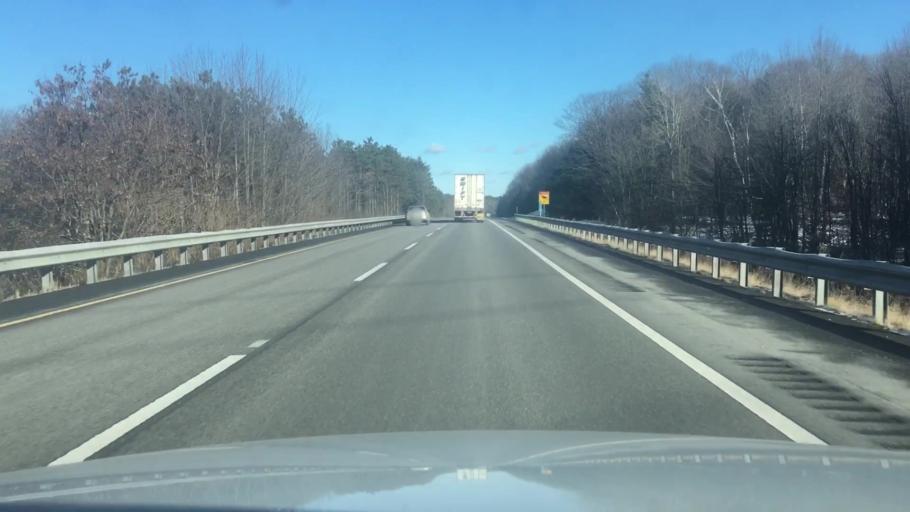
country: US
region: Maine
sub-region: Kennebec County
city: Augusta
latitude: 44.3682
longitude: -69.7750
